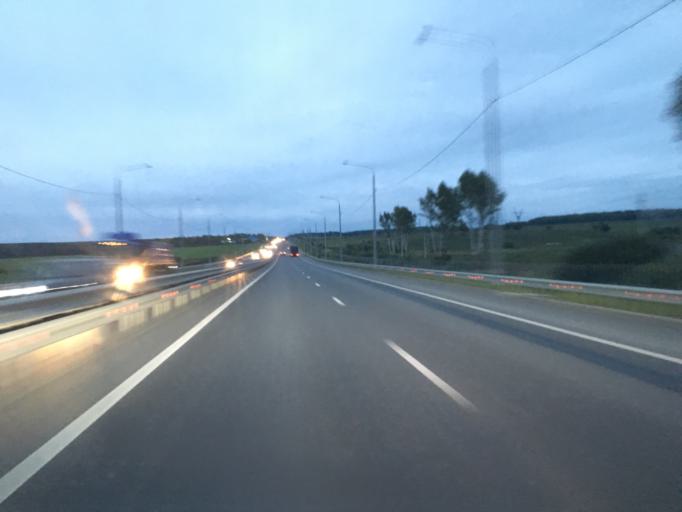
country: RU
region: Kaluga
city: Maloyaroslavets
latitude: 54.9479
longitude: 36.4419
